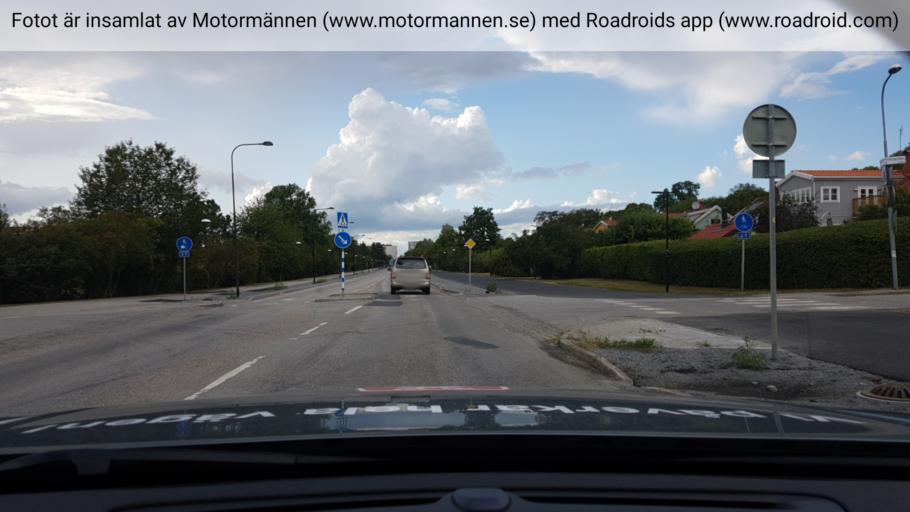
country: SE
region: Stockholm
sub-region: Stockholms Kommun
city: Arsta
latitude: 59.2854
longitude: 18.0672
